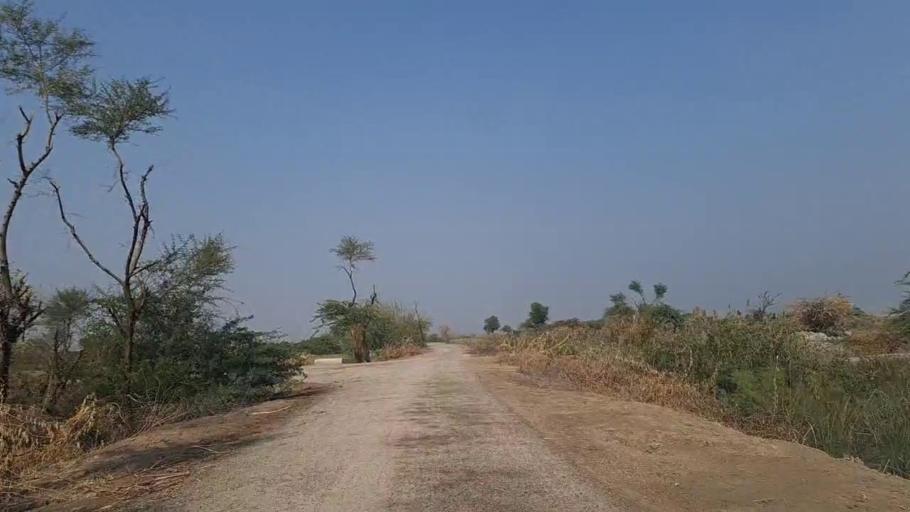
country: PK
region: Sindh
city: Nawabshah
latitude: 26.3696
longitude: 68.4253
